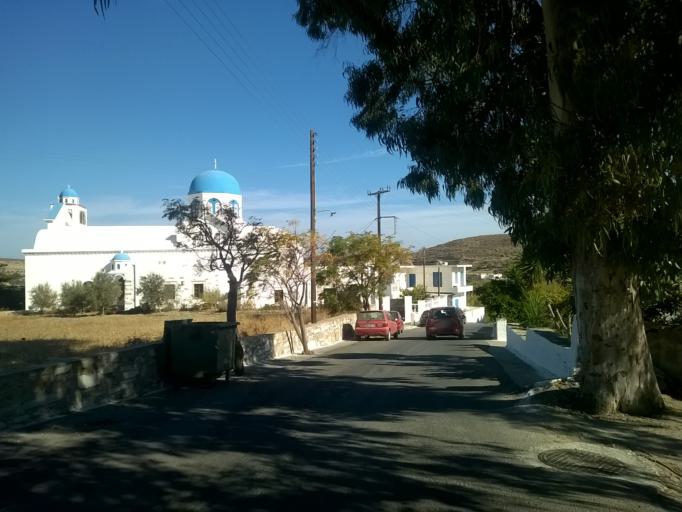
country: GR
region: South Aegean
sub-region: Nomos Kykladon
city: Naxos
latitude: 37.1172
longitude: 25.4359
